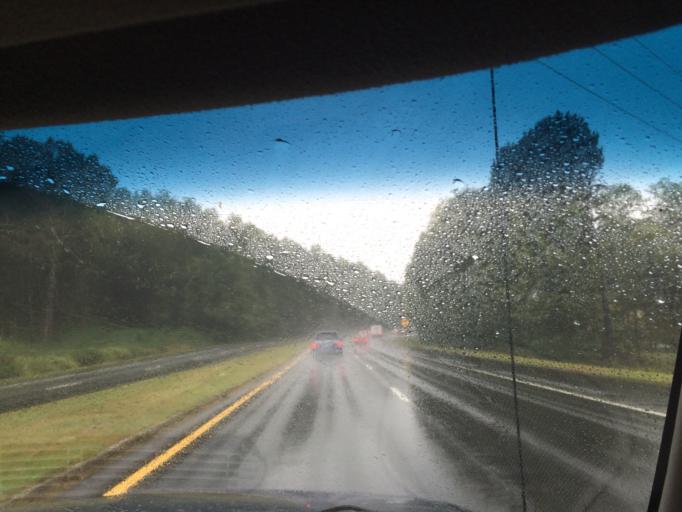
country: US
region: Georgia
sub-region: Cobb County
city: Marietta
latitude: 33.9637
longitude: -84.5114
